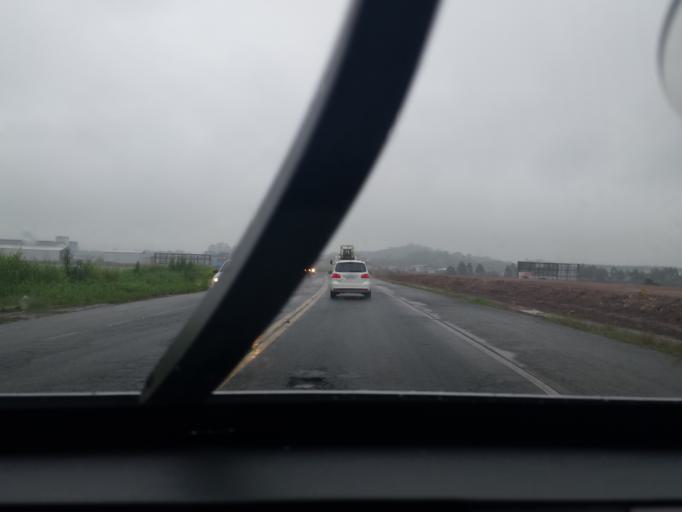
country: BR
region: Santa Catarina
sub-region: Navegantes
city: Navegantes
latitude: -26.8331
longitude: -48.7270
